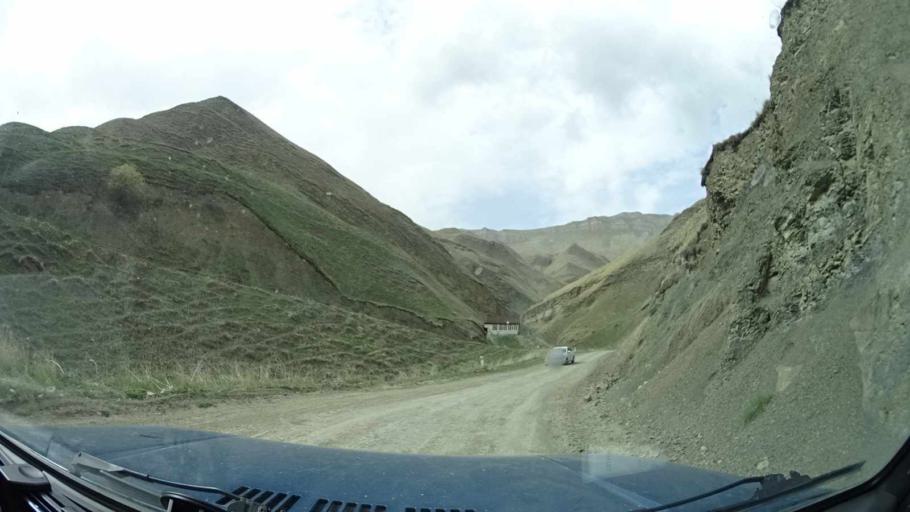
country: RU
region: Dagestan
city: Usisha
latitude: 42.1333
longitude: 47.3679
